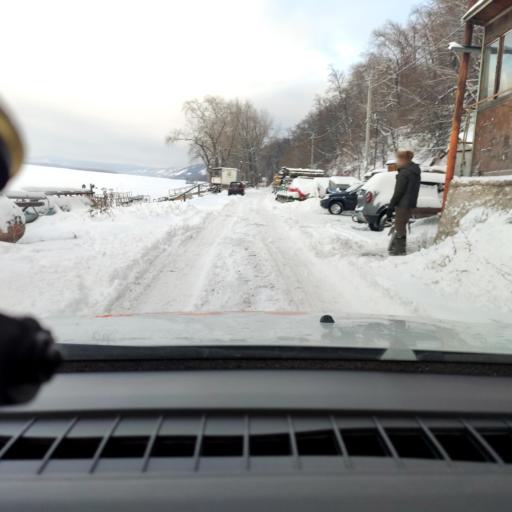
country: RU
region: Samara
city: Samara
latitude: 53.2871
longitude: 50.1909
